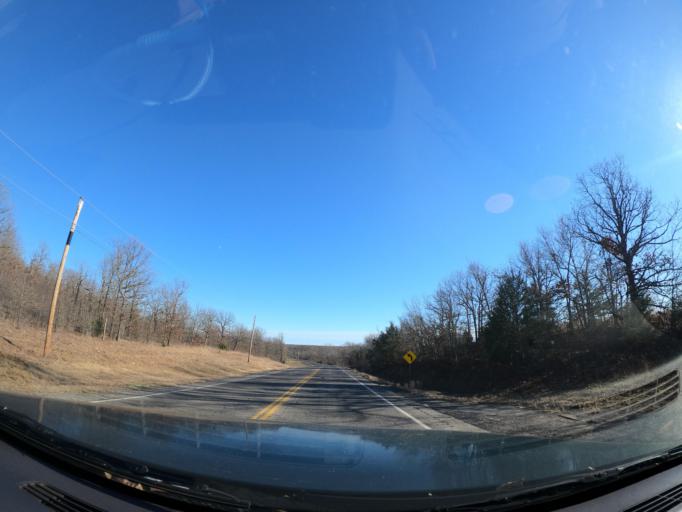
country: US
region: Oklahoma
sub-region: Pittsburg County
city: Longtown
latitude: 35.2168
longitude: -95.4241
